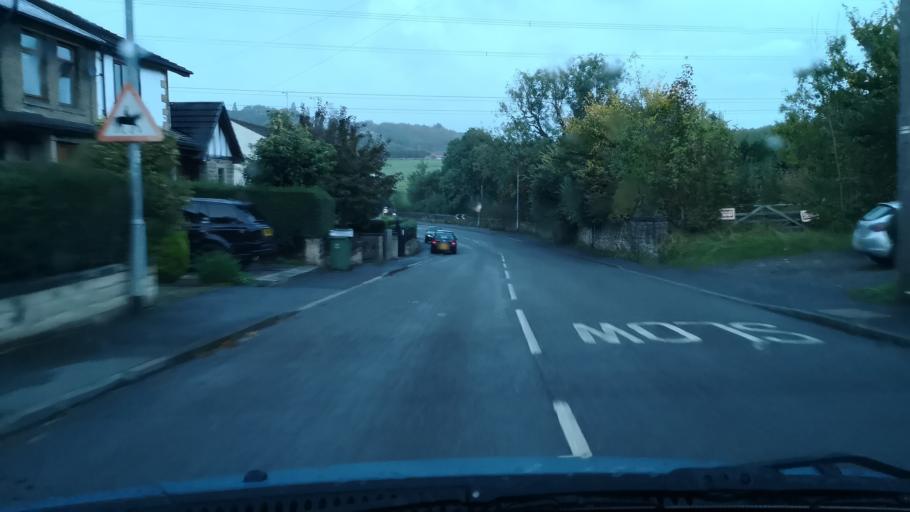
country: GB
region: England
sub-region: Kirklees
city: Batley
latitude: 53.7234
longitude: -1.6281
